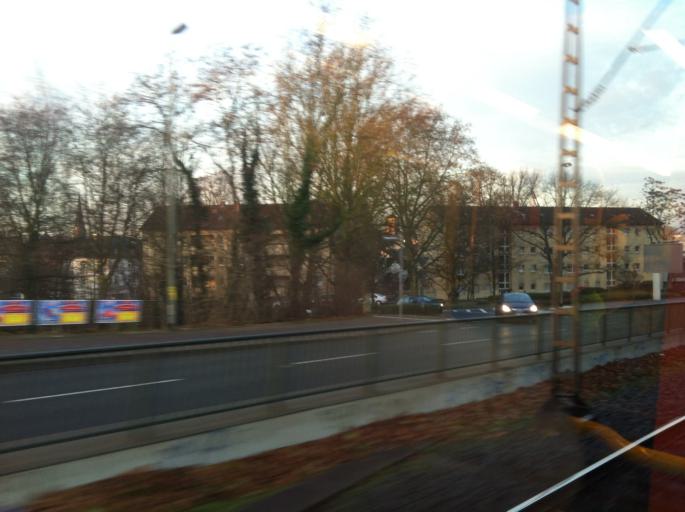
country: DE
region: Hesse
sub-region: Regierungsbezirk Darmstadt
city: Frankfurt am Main
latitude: 50.1596
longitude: 8.6522
